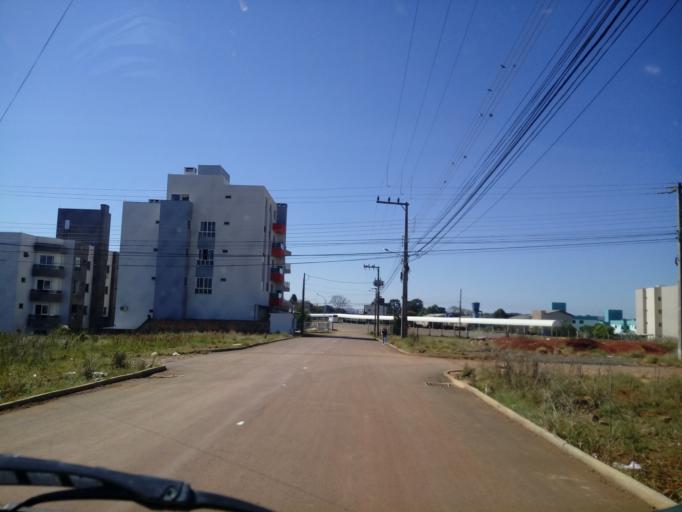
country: BR
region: Santa Catarina
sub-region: Chapeco
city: Chapeco
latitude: -27.0938
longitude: -52.6700
